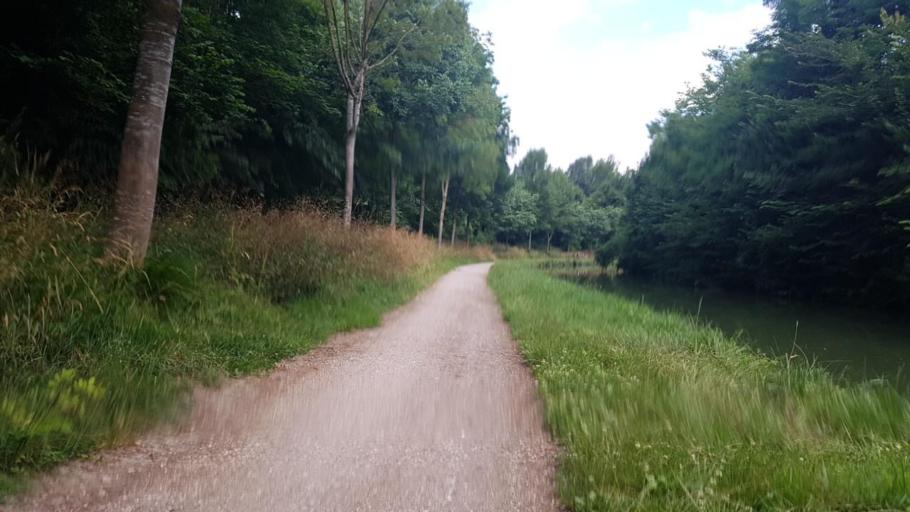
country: FR
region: Ile-de-France
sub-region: Departement de Seine-et-Marne
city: Claye-Souilly
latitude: 48.9539
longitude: 2.6768
